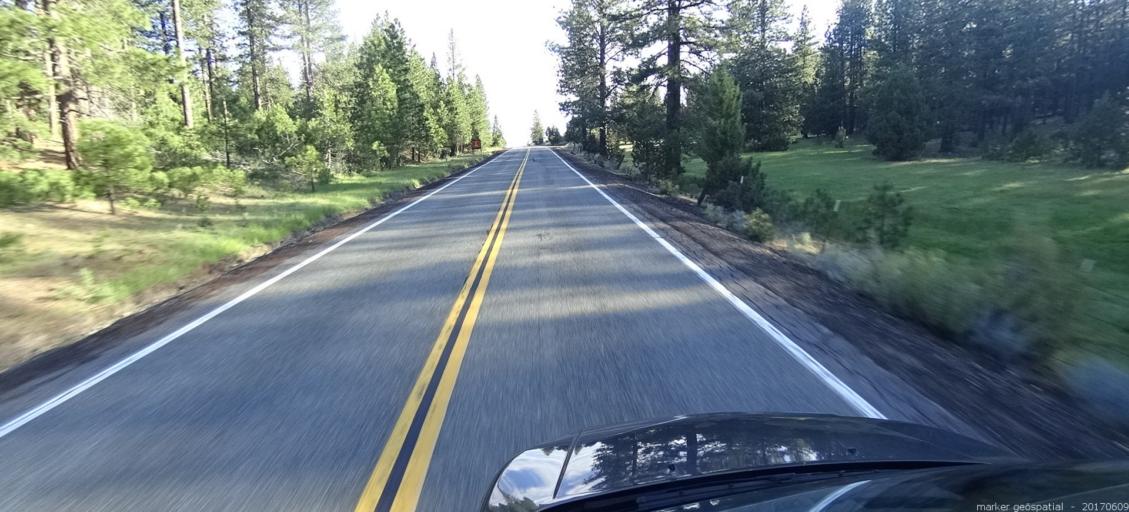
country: US
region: California
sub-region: Siskiyou County
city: Weed
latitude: 41.4337
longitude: -122.6390
